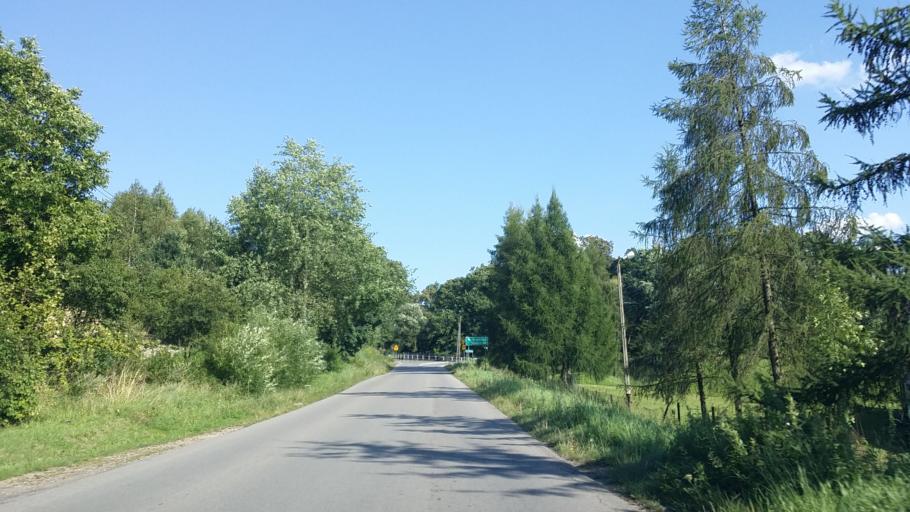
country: PL
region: Lesser Poland Voivodeship
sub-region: Powiat wadowicki
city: Witanowice
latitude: 49.9194
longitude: 19.5083
